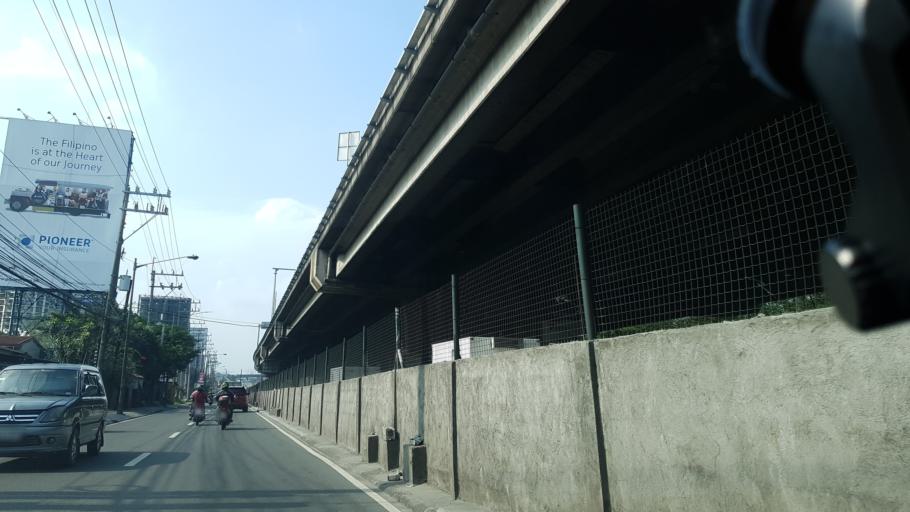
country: PH
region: Metro Manila
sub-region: Makati City
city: Makati City
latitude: 14.5035
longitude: 121.0366
